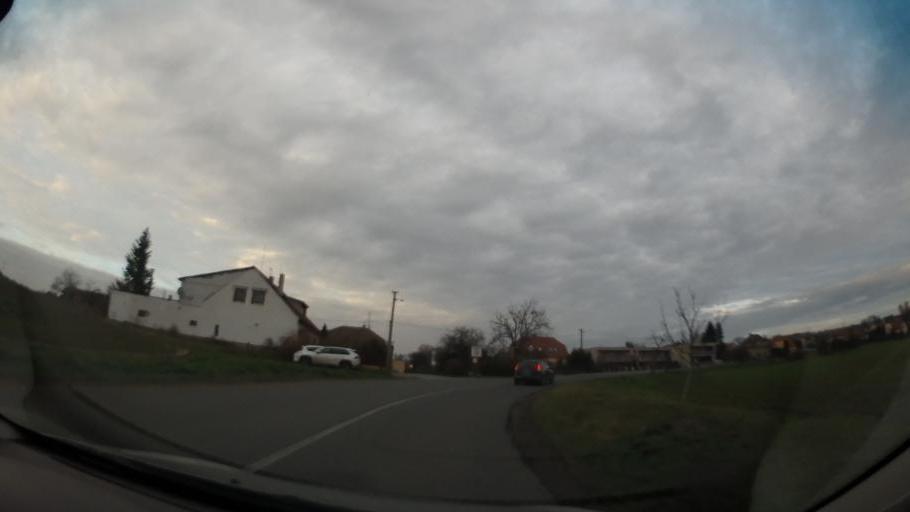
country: CZ
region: South Moravian
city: Oslavany
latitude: 49.1326
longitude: 16.3509
